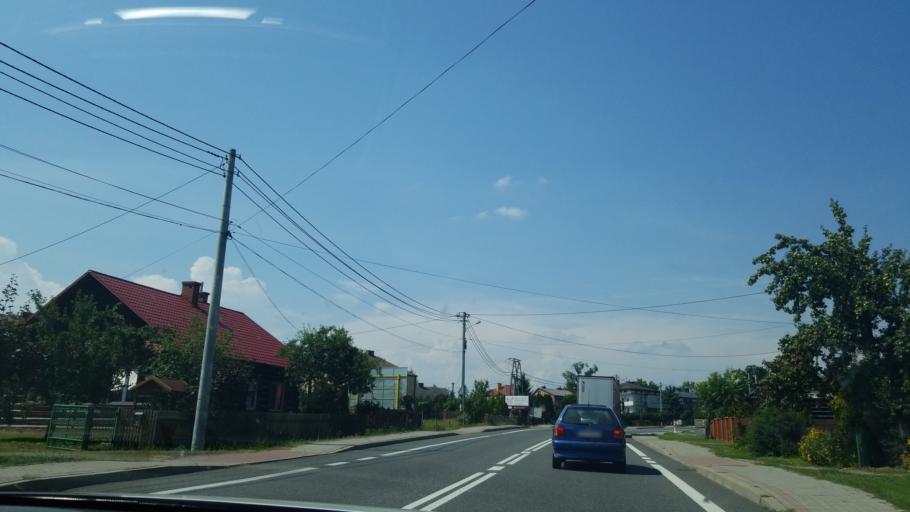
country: PL
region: Subcarpathian Voivodeship
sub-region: Powiat rzeszowski
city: Kamien
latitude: 50.3441
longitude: 22.1306
